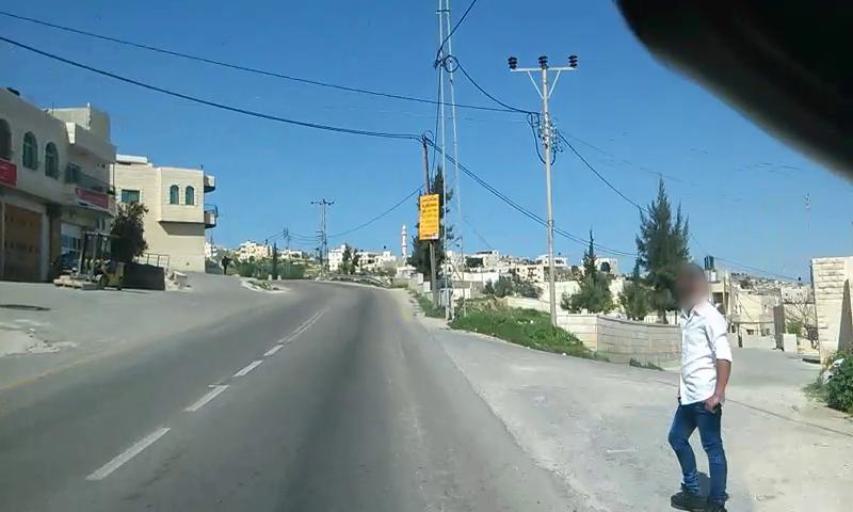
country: PS
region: West Bank
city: Jannatah
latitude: 31.6521
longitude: 35.2114
